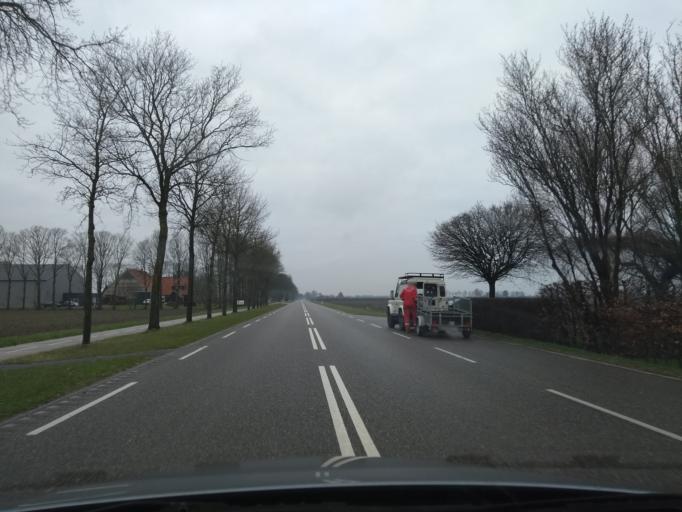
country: NL
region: Overijssel
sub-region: Gemeente Steenwijkerland
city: Vollenhove
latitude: 52.6967
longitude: 5.9127
